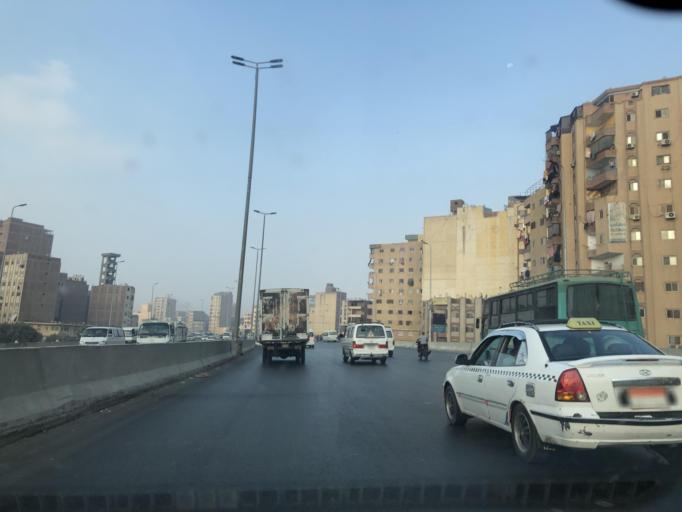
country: EG
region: Al Jizah
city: Awsim
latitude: 30.0780
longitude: 31.1804
